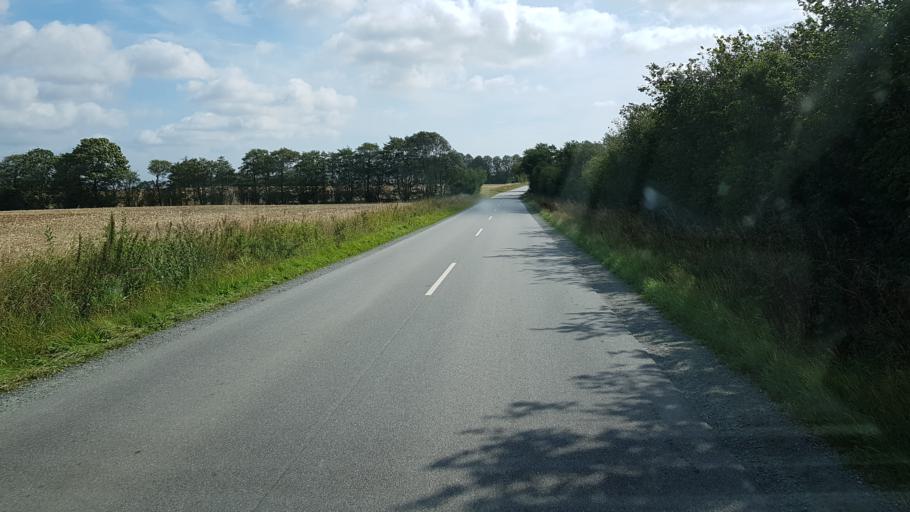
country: DK
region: South Denmark
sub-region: Haderslev Kommune
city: Haderslev
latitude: 55.3068
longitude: 9.5265
